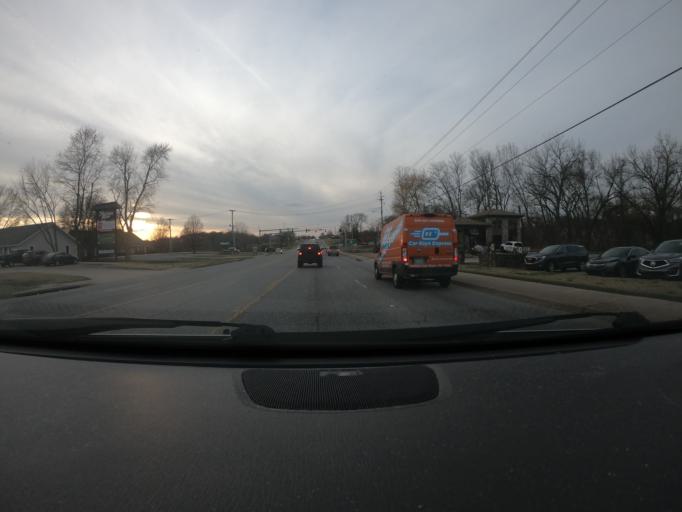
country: US
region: Arkansas
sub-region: Benton County
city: Rogers
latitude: 36.3344
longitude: -94.1603
